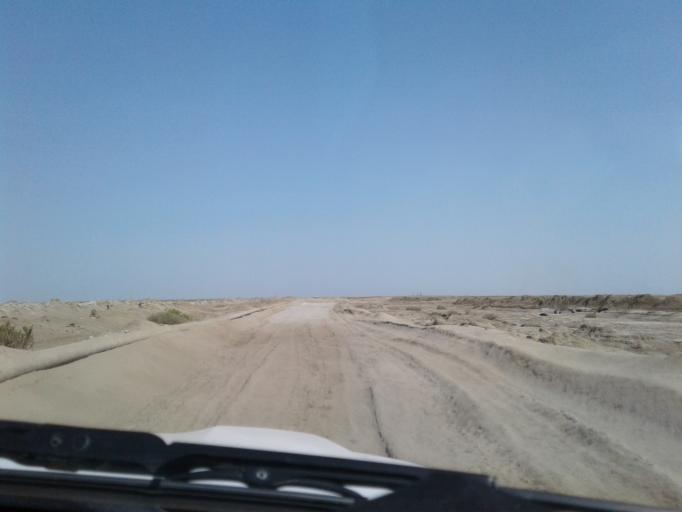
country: IR
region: Golestan
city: Gomishan
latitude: 37.8309
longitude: 53.9215
